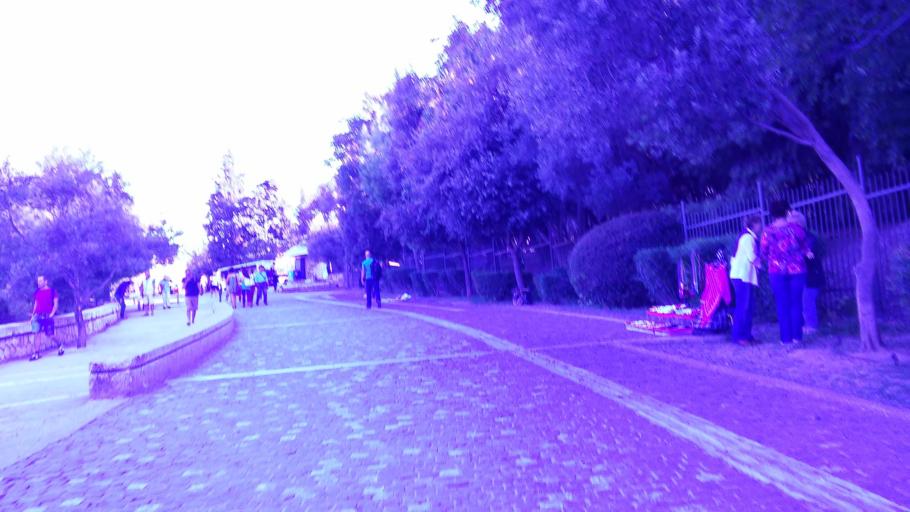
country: GR
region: Attica
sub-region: Nomarchia Athinas
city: Athens
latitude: 37.9707
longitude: 23.7214
